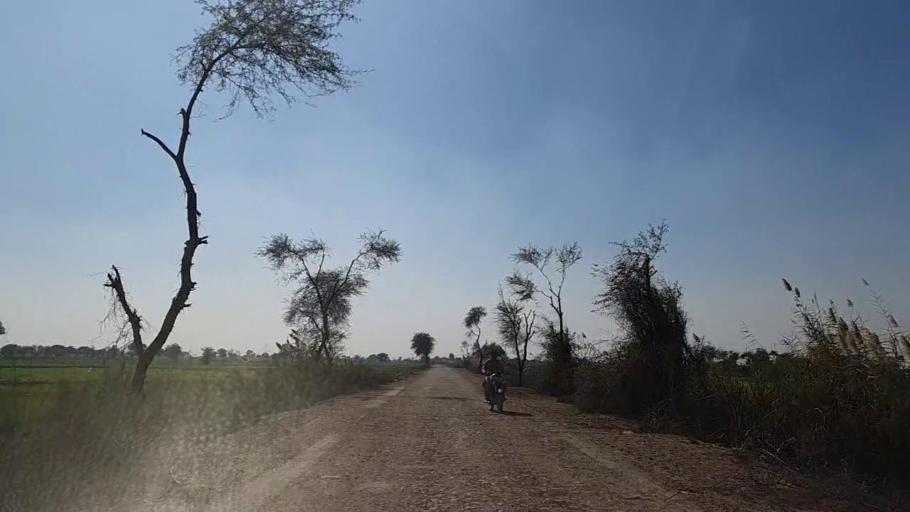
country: PK
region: Sindh
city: Bandhi
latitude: 26.5241
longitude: 68.2896
